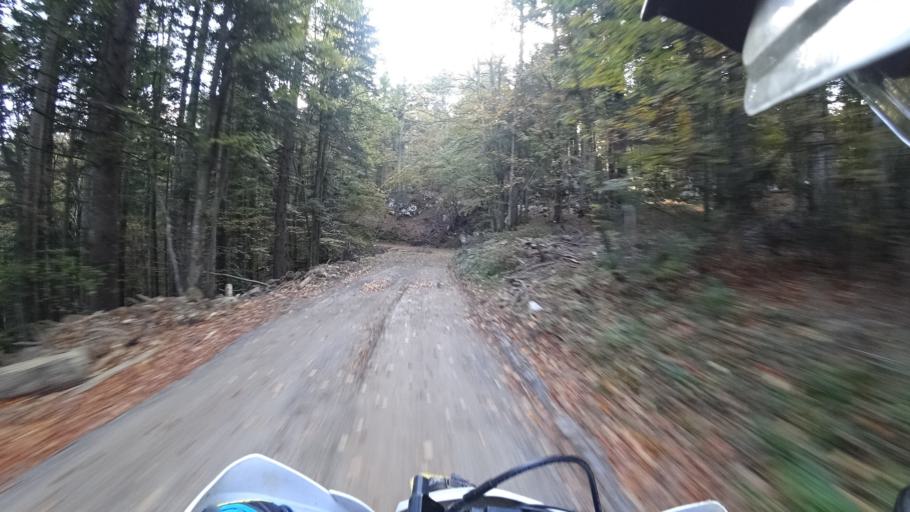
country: HR
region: Karlovacka
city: Plaski
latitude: 44.9475
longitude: 15.4512
